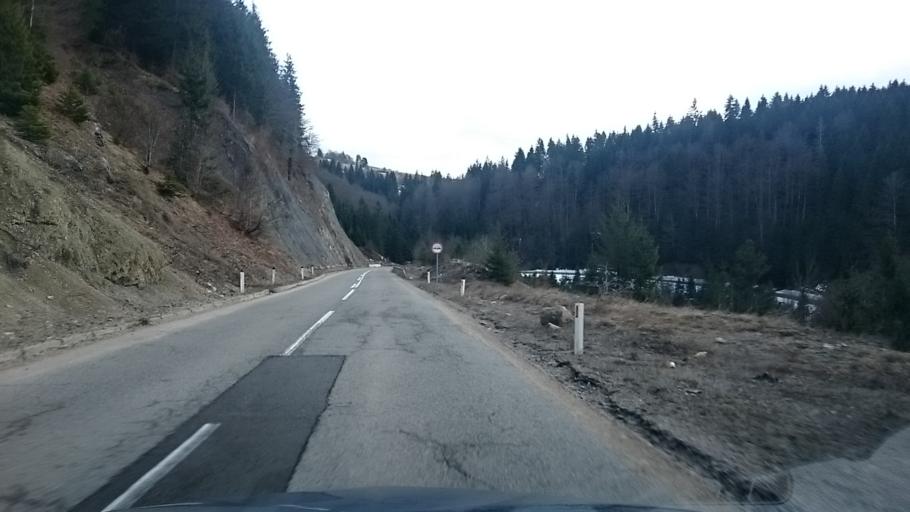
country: BA
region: Republika Srpska
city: Skender Vakuf
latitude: 44.4723
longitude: 17.3879
